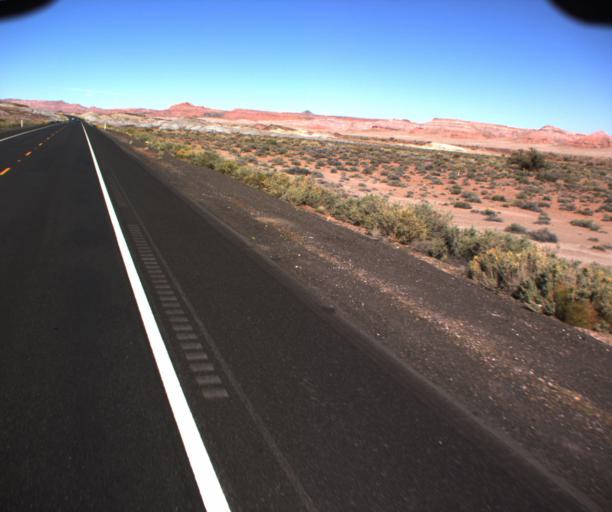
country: US
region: Arizona
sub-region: Coconino County
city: Tuba City
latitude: 36.1126
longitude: -111.3954
